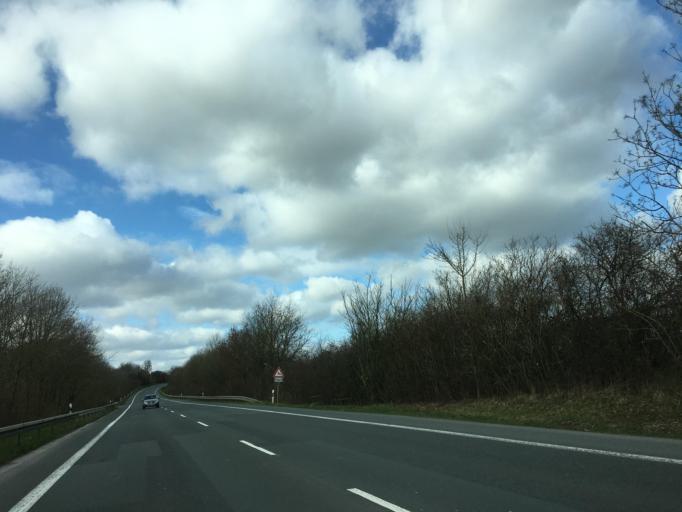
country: DE
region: North Rhine-Westphalia
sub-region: Regierungsbezirk Munster
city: Horstmar
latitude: 52.0734
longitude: 7.3062
